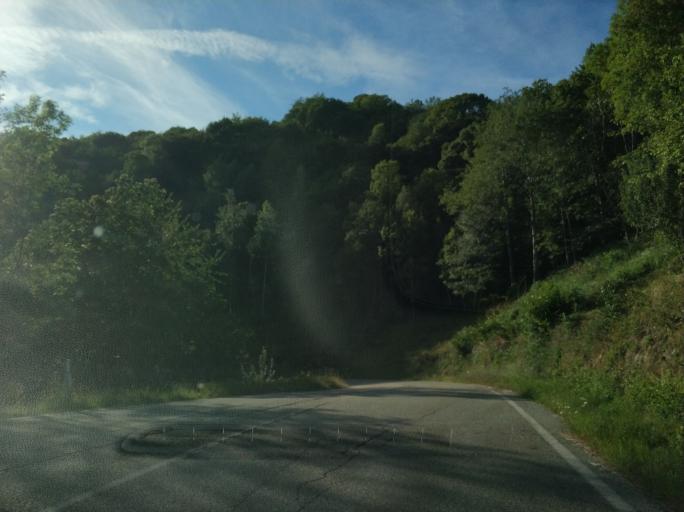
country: IT
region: Piedmont
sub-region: Provincia di Torino
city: Monastero di Lanzo
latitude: 45.3051
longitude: 7.4426
